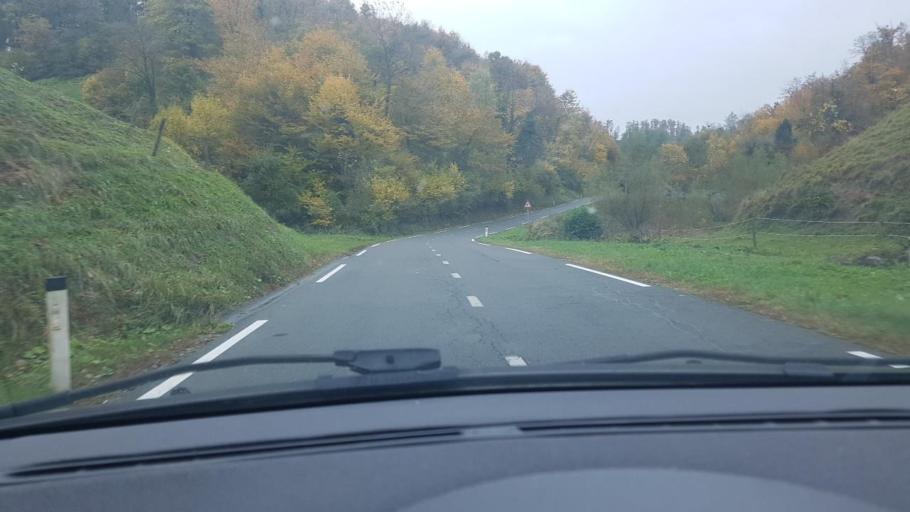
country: SI
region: Rogatec
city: Rogatec
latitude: 46.2701
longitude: 15.7125
